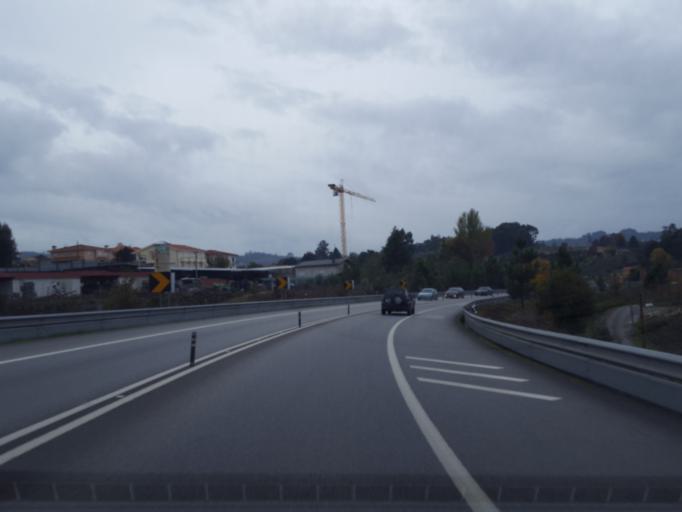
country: PT
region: Porto
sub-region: Marco de Canaveses
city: Marco de Canavezes
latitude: 41.2169
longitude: -8.1802
